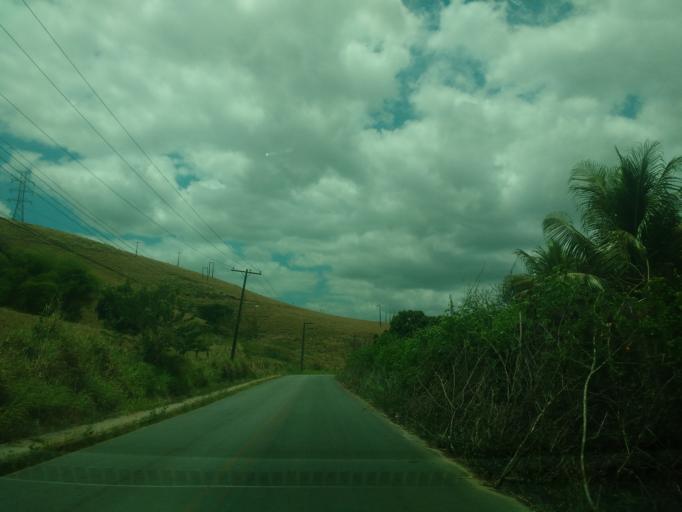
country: BR
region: Alagoas
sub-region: Uniao Dos Palmares
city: Uniao dos Palmares
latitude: -9.1459
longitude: -36.0377
